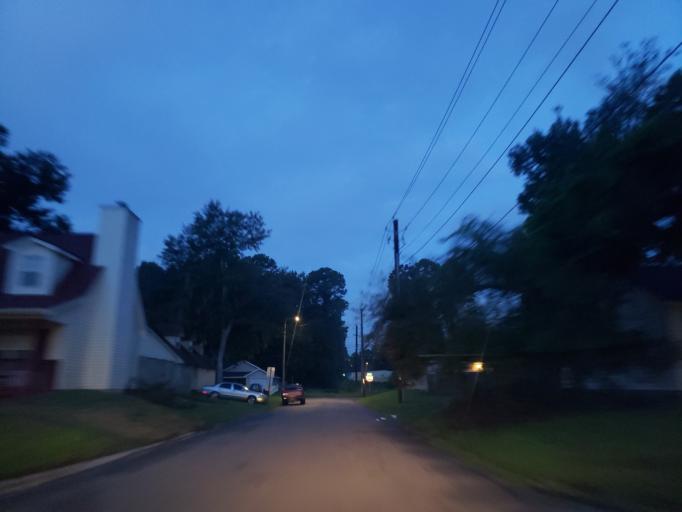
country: US
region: Georgia
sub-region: Chatham County
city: Isle of Hope
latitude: 31.9939
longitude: -81.0749
